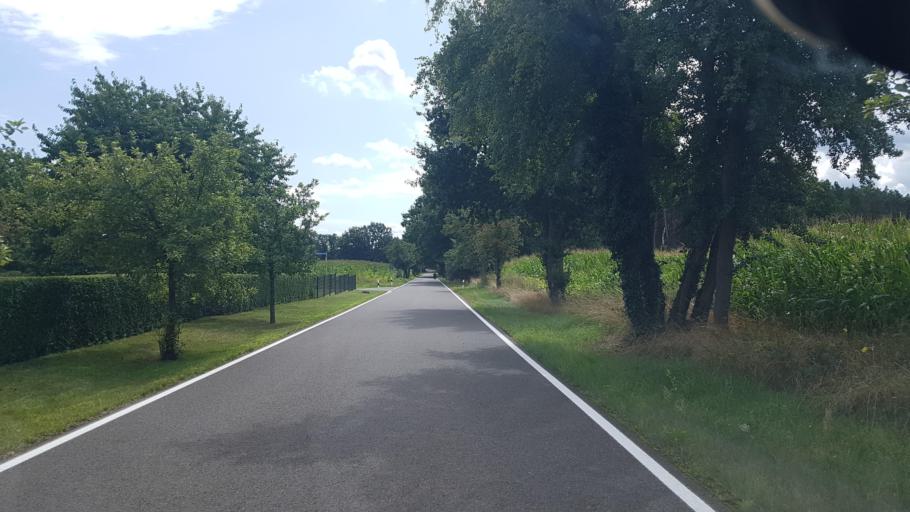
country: DE
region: Brandenburg
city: Spremberg
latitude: 51.5930
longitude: 14.3452
